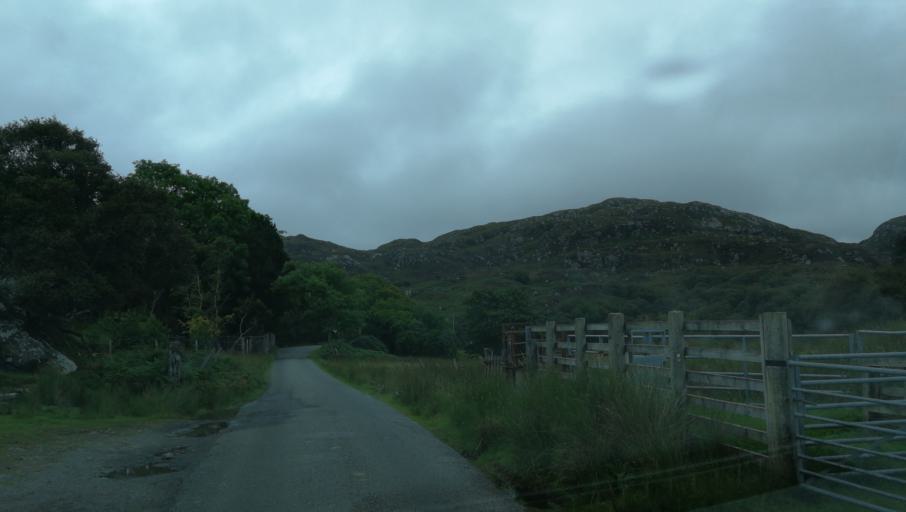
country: GB
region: Scotland
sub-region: Highland
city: Ullapool
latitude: 58.1362
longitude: -5.2511
